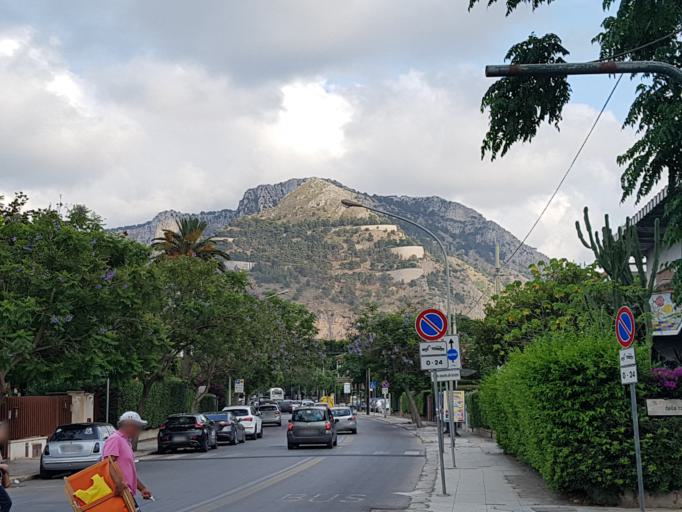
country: IT
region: Sicily
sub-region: Palermo
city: Palermo
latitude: 38.2004
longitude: 13.3266
